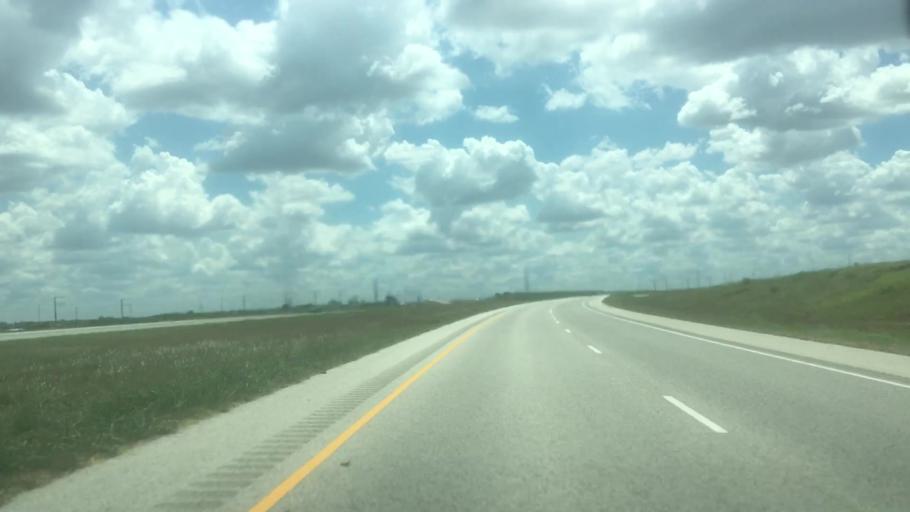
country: US
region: Texas
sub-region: Caldwell County
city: Uhland
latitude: 30.0206
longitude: -97.6876
